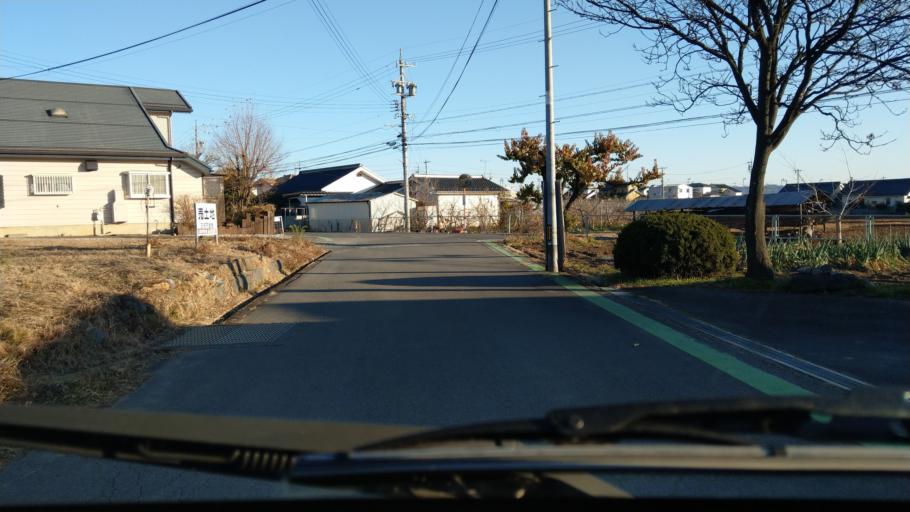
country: JP
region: Nagano
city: Ueda
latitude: 36.3989
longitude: 138.2807
